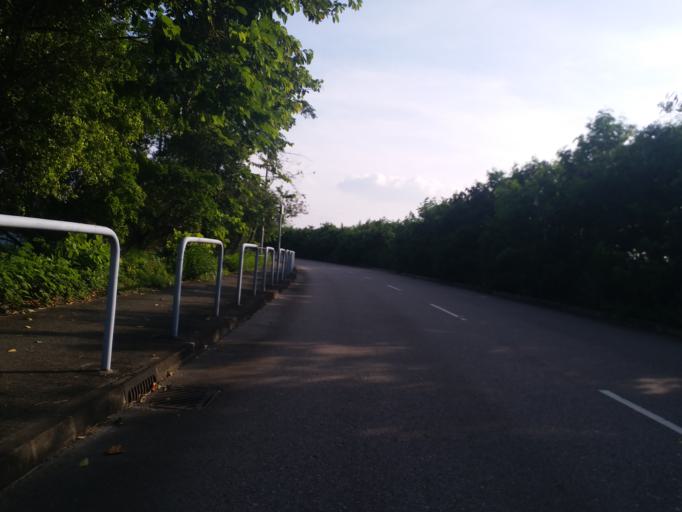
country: HK
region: Yuen Long
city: Yuen Long Kau Hui
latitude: 22.4781
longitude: 114.0524
